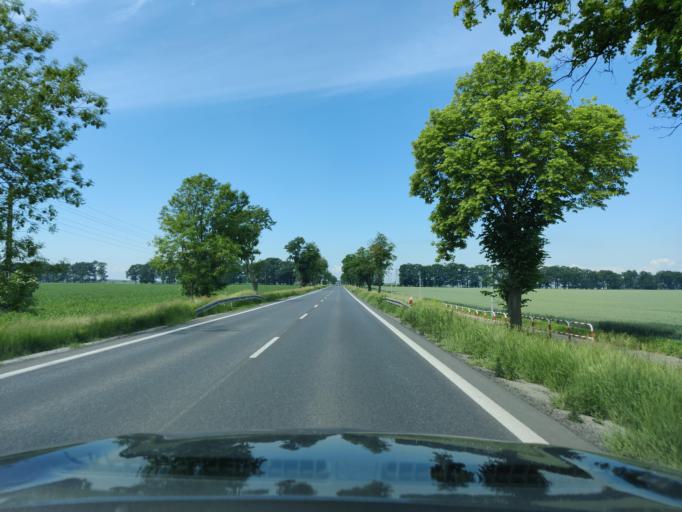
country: PL
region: Greater Poland Voivodeship
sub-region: Powiat grodziski
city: Granowo
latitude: 52.2244
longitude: 16.4817
